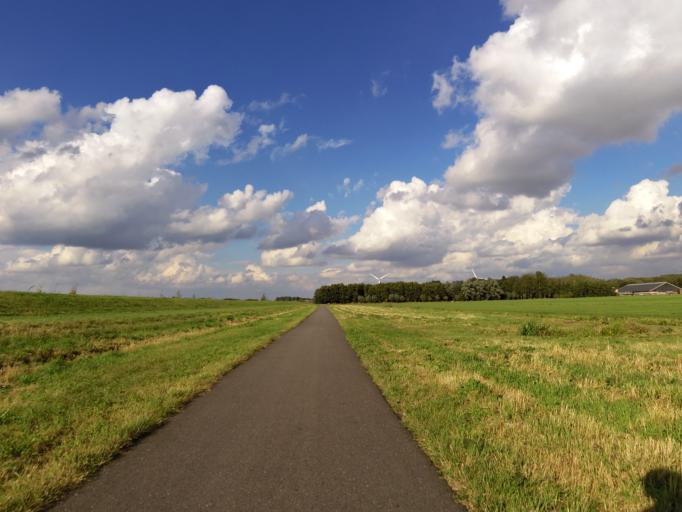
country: NL
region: South Holland
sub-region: Gemeente Alphen aan den Rijn
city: Alphen aan den Rijn
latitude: 52.1093
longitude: 4.6015
